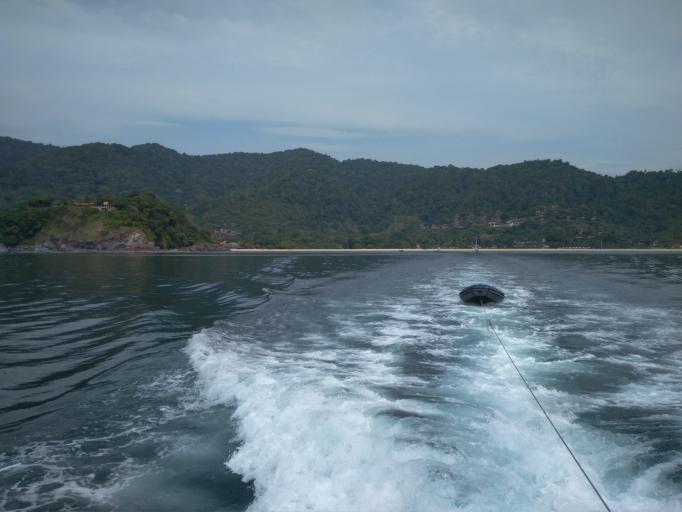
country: TH
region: Krabi
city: Ko Lanta
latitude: 7.4932
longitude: 99.0670
